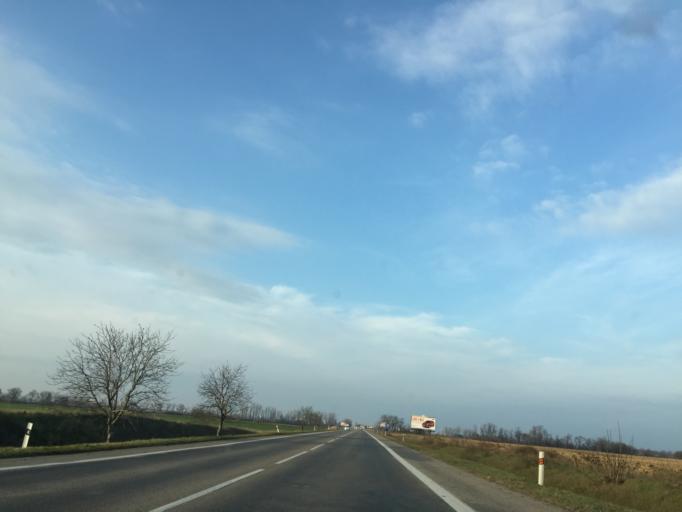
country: SK
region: Nitriansky
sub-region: Okres Nove Zamky
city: Nove Zamky
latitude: 47.9410
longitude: 18.1994
